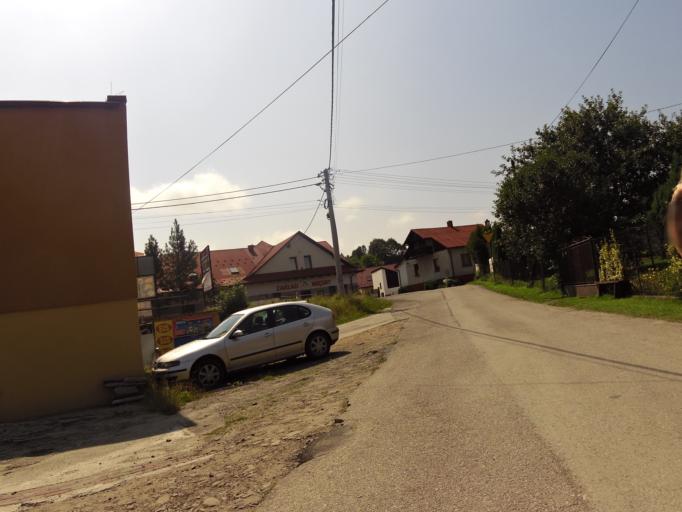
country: PL
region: Silesian Voivodeship
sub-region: Powiat zywiecki
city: Rajcza
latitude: 49.5020
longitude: 19.0970
